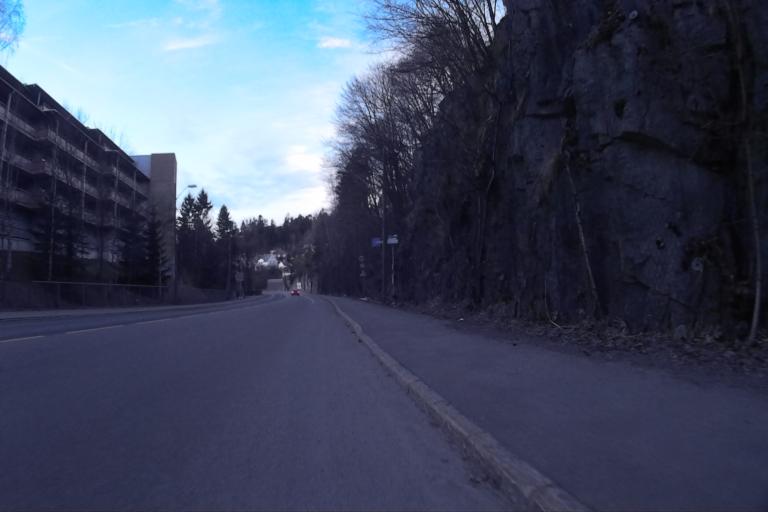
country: NO
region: Oslo
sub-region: Oslo
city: Oslo
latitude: 59.9015
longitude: 10.8249
